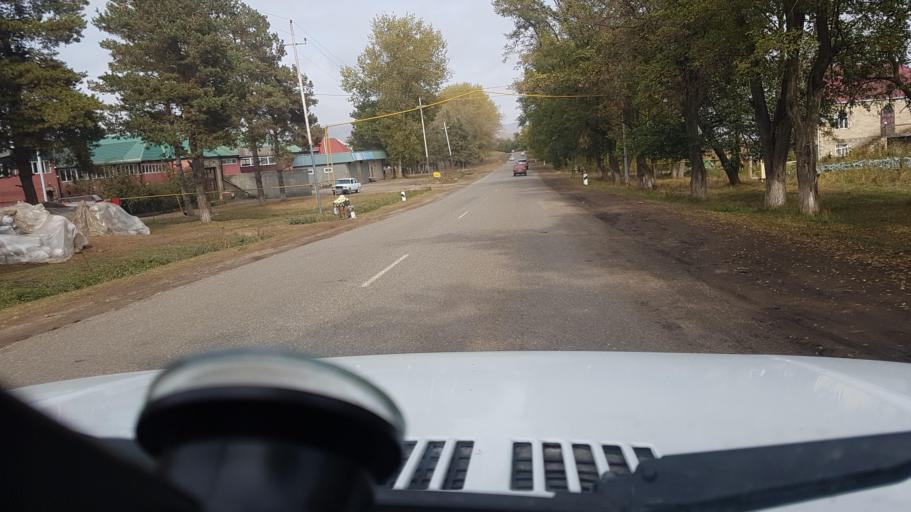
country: AZ
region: Gadabay Rayon
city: Ariqdam
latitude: 40.6419
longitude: 45.8129
